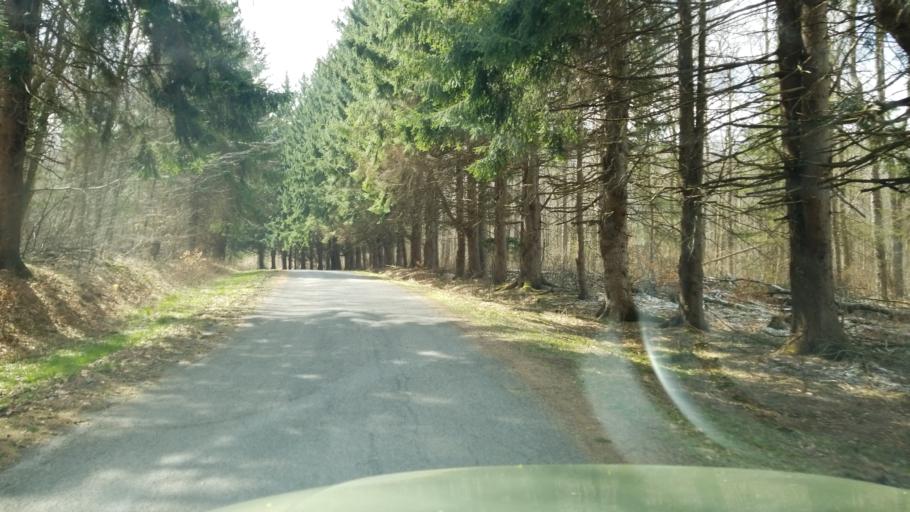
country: US
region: Pennsylvania
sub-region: Jefferson County
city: Brockway
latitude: 41.2871
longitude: -78.8760
